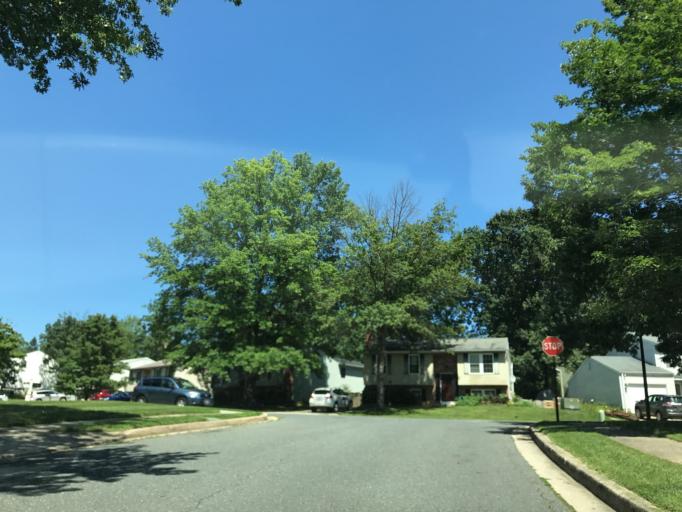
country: US
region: Maryland
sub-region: Baltimore County
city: Perry Hall
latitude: 39.3834
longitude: -76.4655
